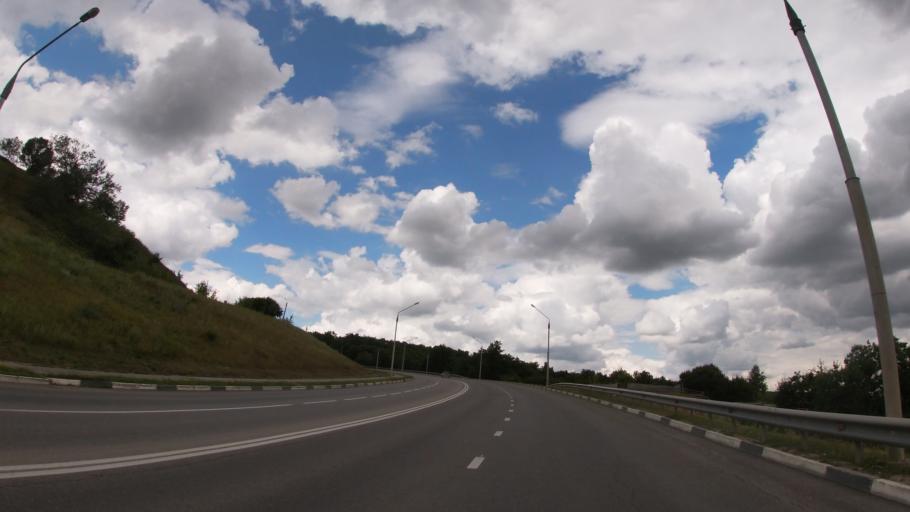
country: RU
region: Belgorod
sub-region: Belgorodskiy Rayon
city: Belgorod
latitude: 50.6193
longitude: 36.6164
